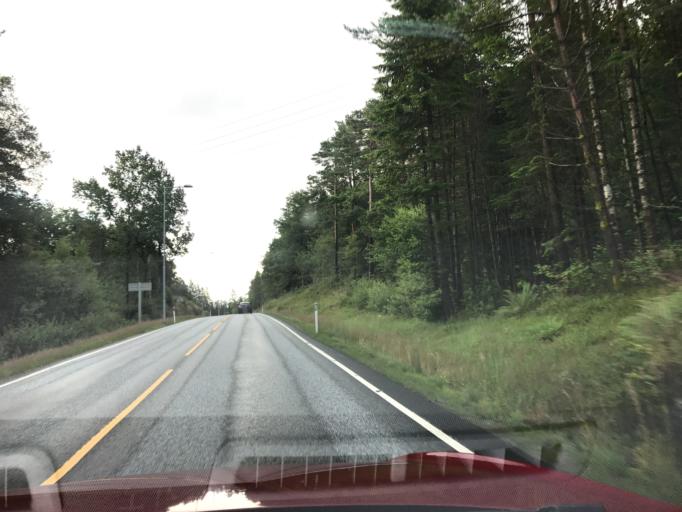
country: NO
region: Hordaland
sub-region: Stord
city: Leirvik
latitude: 59.7866
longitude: 5.4847
